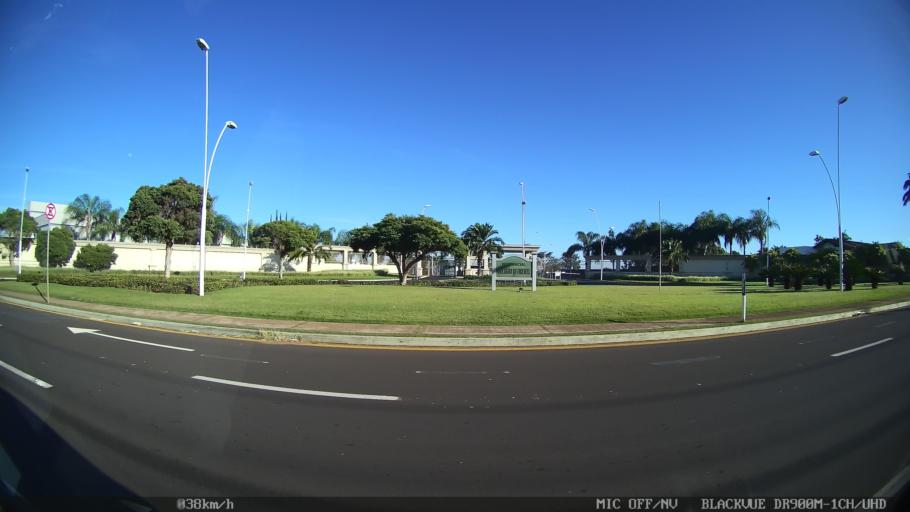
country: BR
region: Sao Paulo
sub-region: Franca
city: Franca
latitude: -20.5696
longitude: -47.4059
